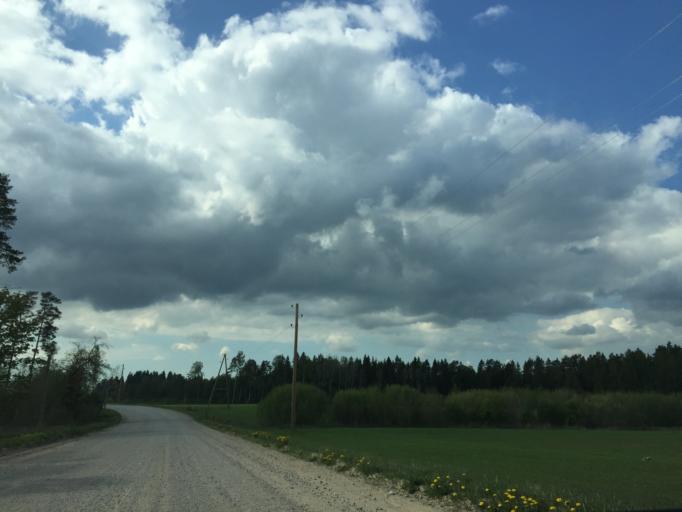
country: LV
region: Krimulda
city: Ragana
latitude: 57.2926
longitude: 24.8051
